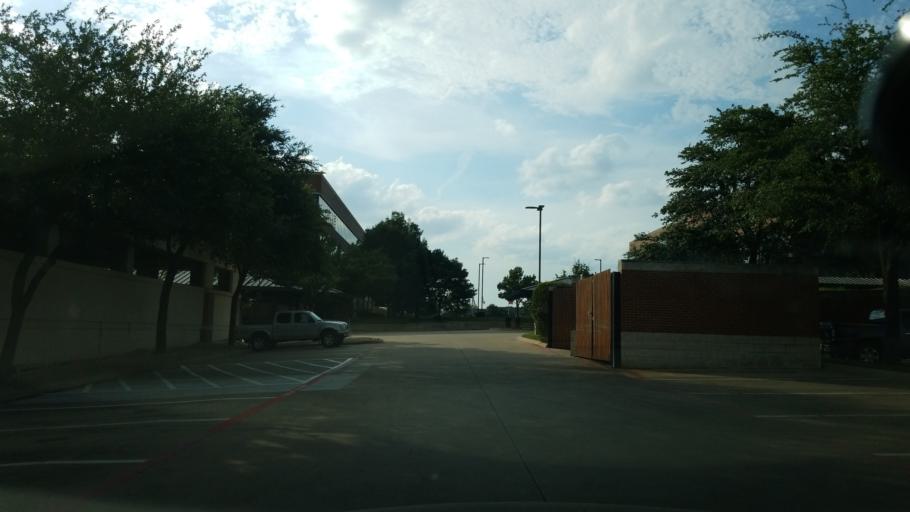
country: US
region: Texas
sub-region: Dallas County
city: Farmers Branch
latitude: 32.8991
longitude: -96.9622
